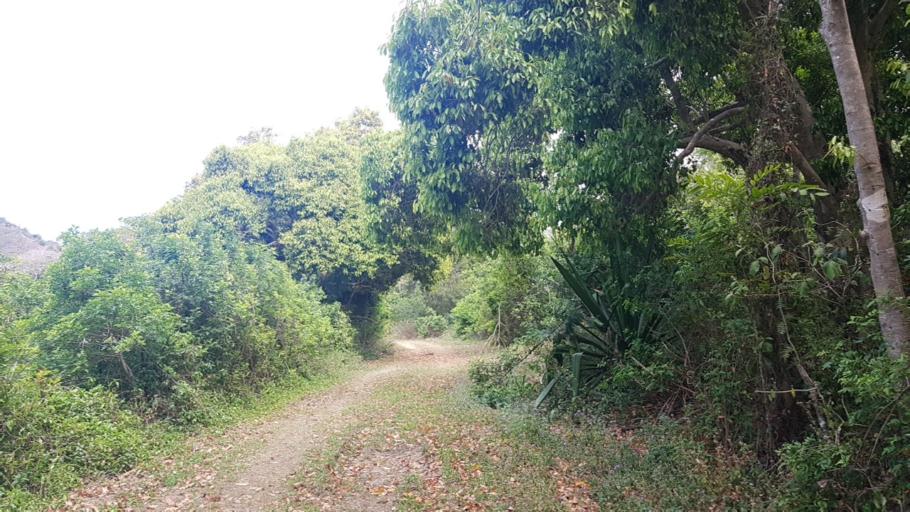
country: NC
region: South Province
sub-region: Dumbea
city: Dumbea
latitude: -22.1760
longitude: 166.4748
